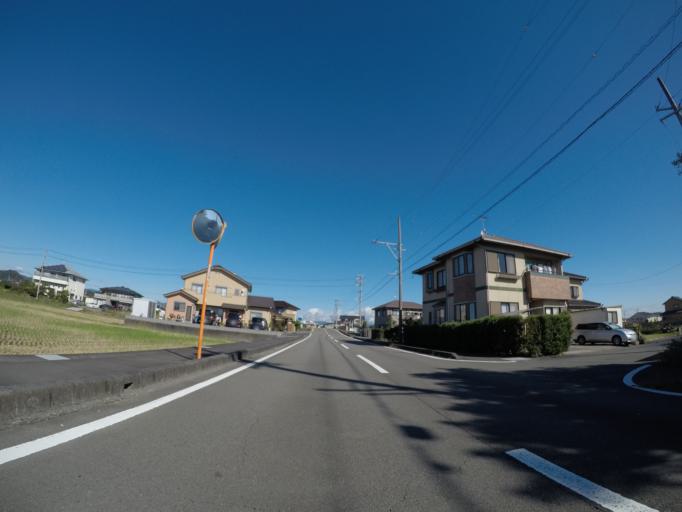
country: JP
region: Shizuoka
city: Fujieda
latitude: 34.8384
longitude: 138.2397
